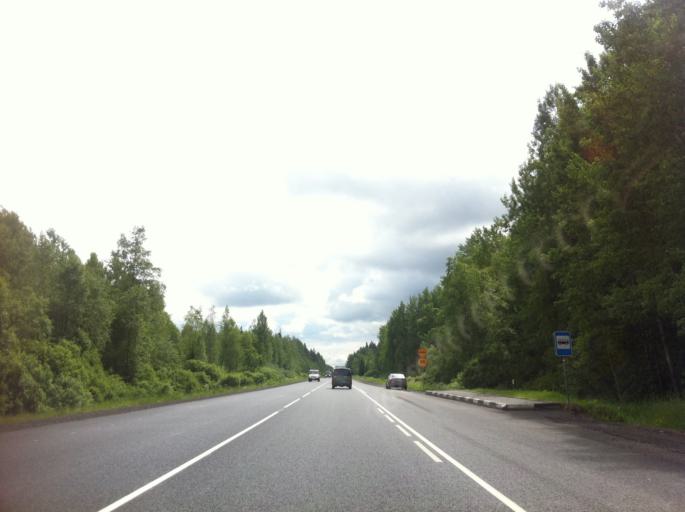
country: RU
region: Leningrad
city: Rozhdestveno
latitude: 59.2302
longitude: 29.9279
